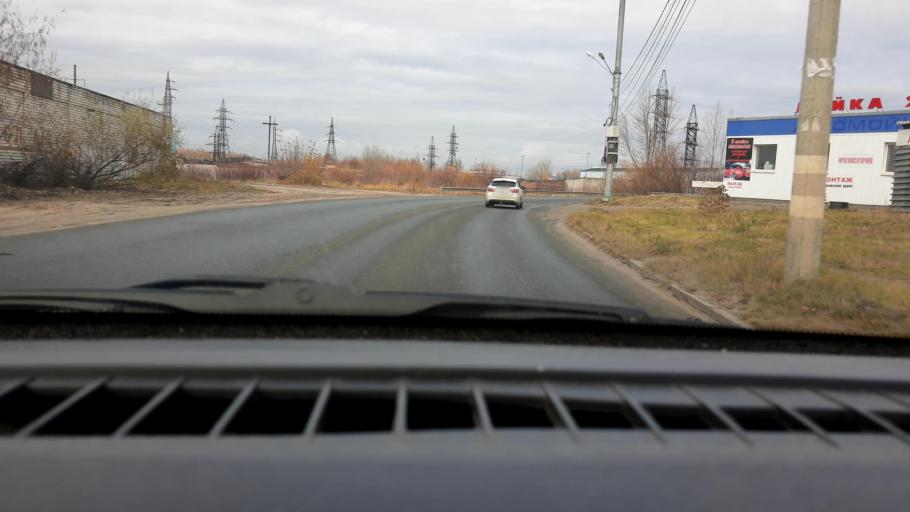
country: RU
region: Nizjnij Novgorod
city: Gorbatovka
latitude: 56.3605
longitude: 43.7951
